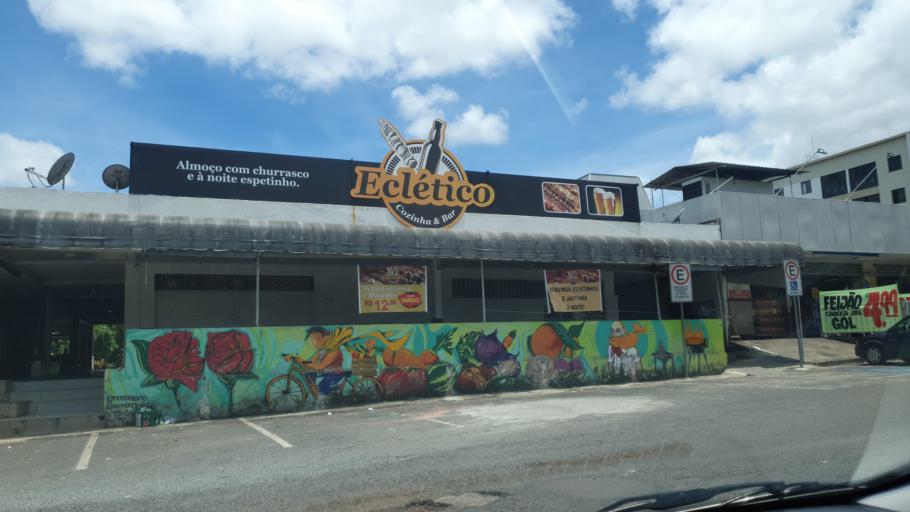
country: BR
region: Federal District
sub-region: Brasilia
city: Brasilia
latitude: -15.7915
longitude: -47.9360
